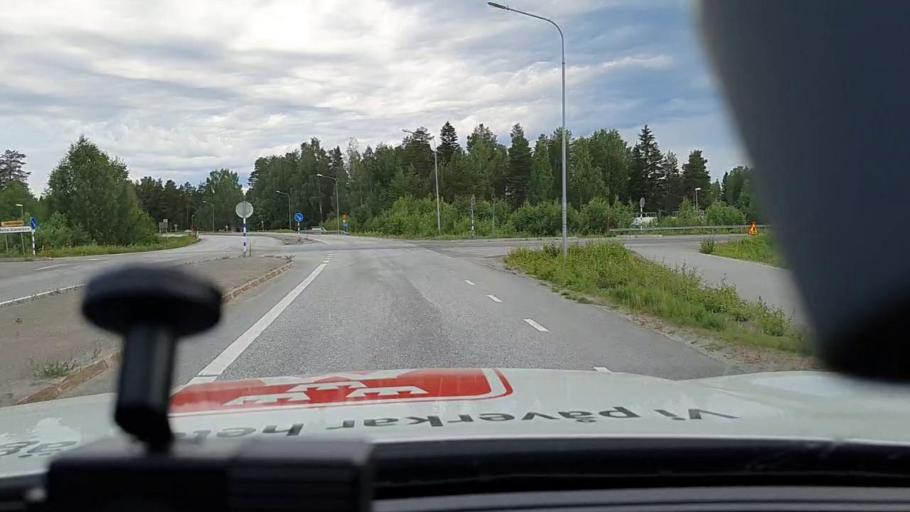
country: SE
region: Norrbotten
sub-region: Bodens Kommun
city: Boden
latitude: 65.8140
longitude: 21.6487
